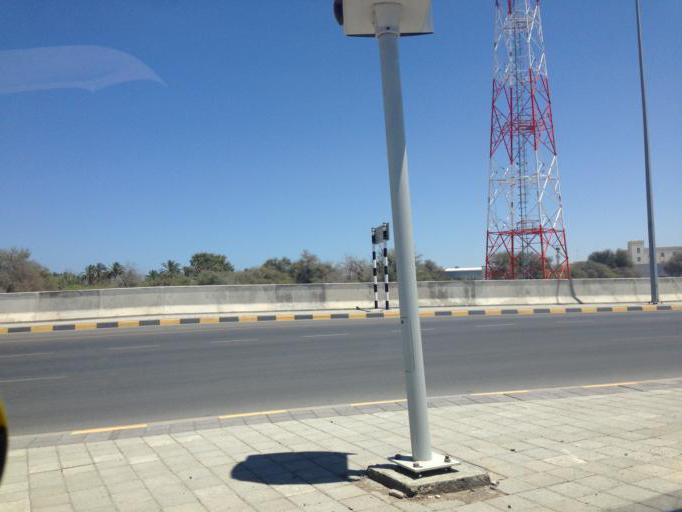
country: OM
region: Muhafazat Masqat
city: As Sib al Jadidah
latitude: 23.6610
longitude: 58.2041
